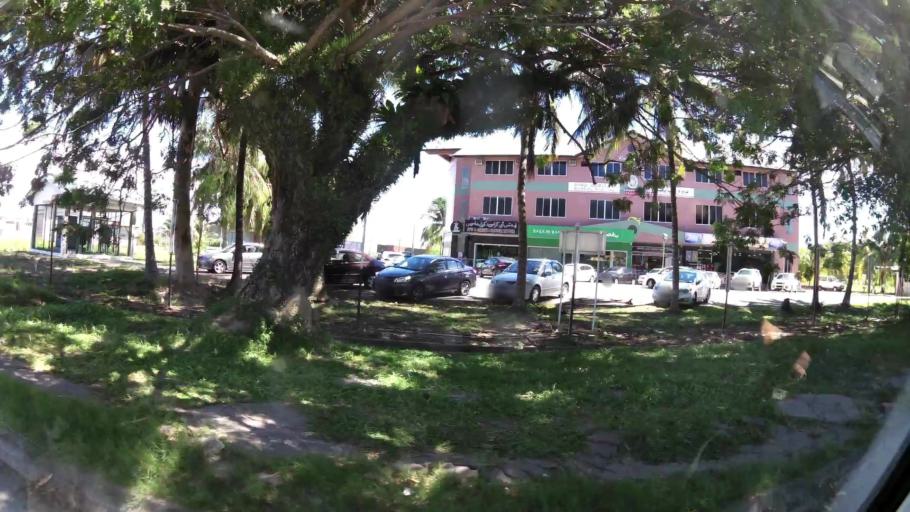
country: BN
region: Brunei and Muara
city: Bandar Seri Begawan
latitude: 5.0270
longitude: 115.0686
